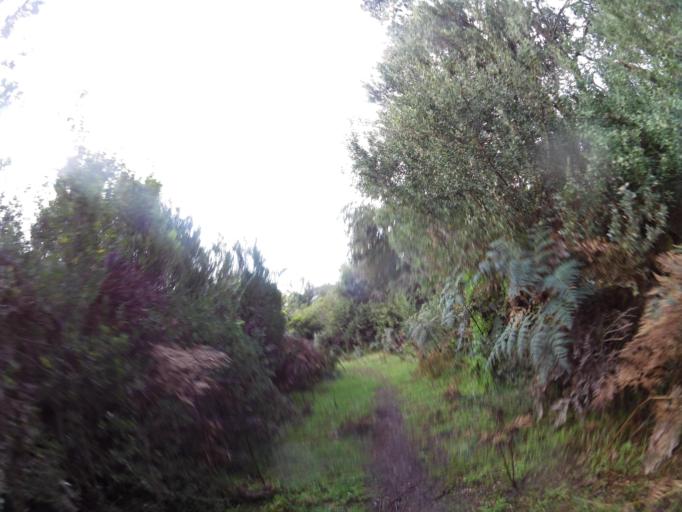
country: AU
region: Victoria
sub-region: Bass Coast
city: North Wonthaggi
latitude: -38.6414
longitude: 145.5629
